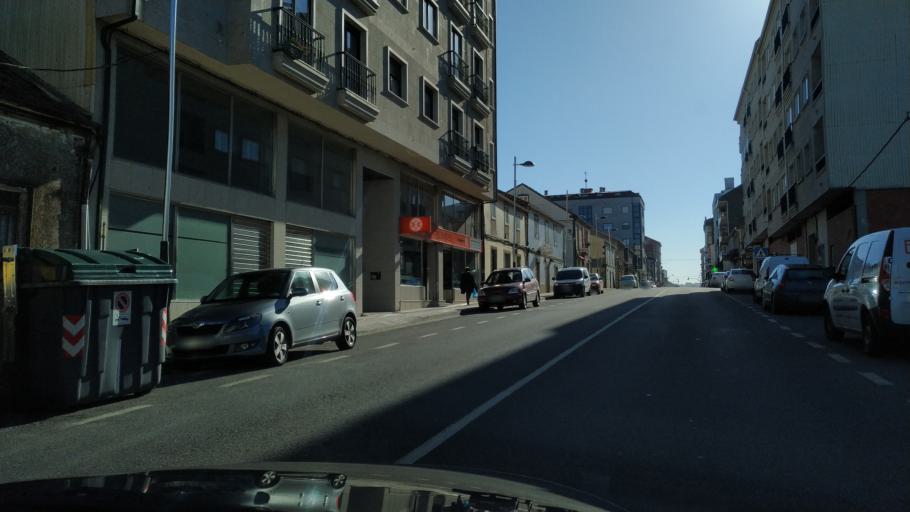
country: ES
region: Galicia
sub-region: Provincia de Pontevedra
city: Silleda
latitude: 42.7308
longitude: -8.3054
